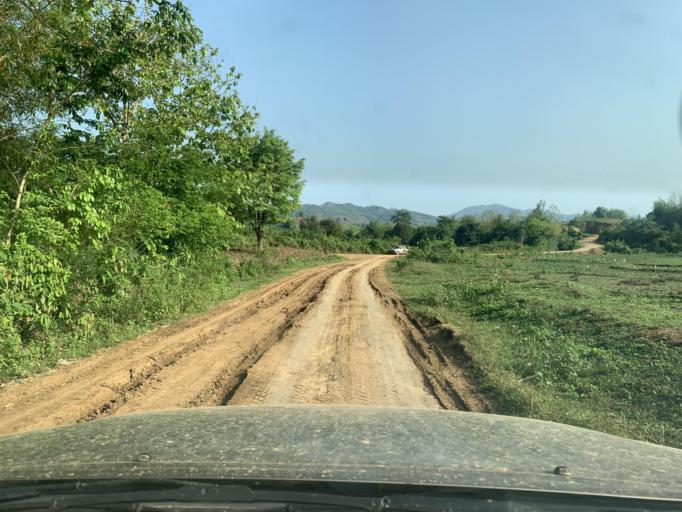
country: TH
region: Uttaradit
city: Ban Khok
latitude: 18.2701
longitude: 101.3095
